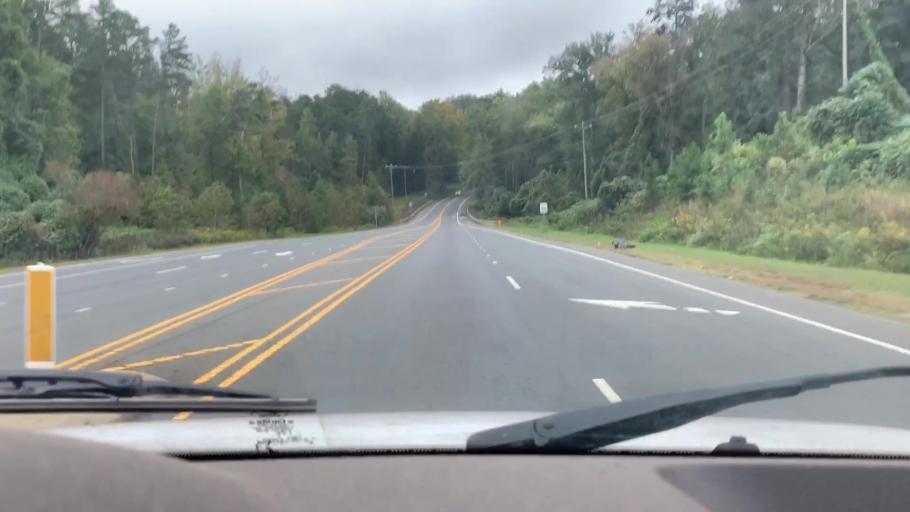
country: US
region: North Carolina
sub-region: Mecklenburg County
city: Huntersville
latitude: 35.3634
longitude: -80.8255
